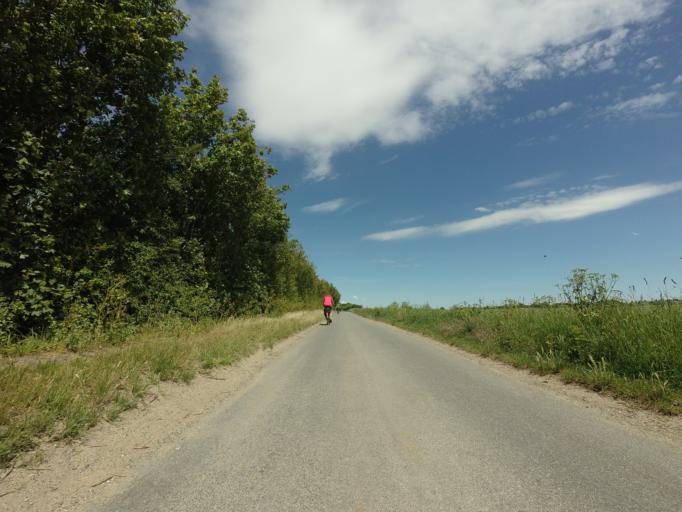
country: GB
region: England
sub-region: Kent
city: Cliffe
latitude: 51.4541
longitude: 0.4906
